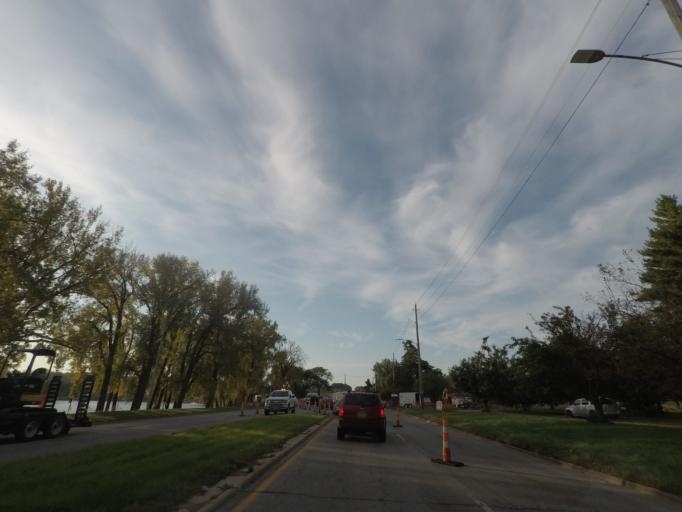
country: US
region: Iowa
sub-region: Polk County
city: Des Moines
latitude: 41.5710
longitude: -93.6450
